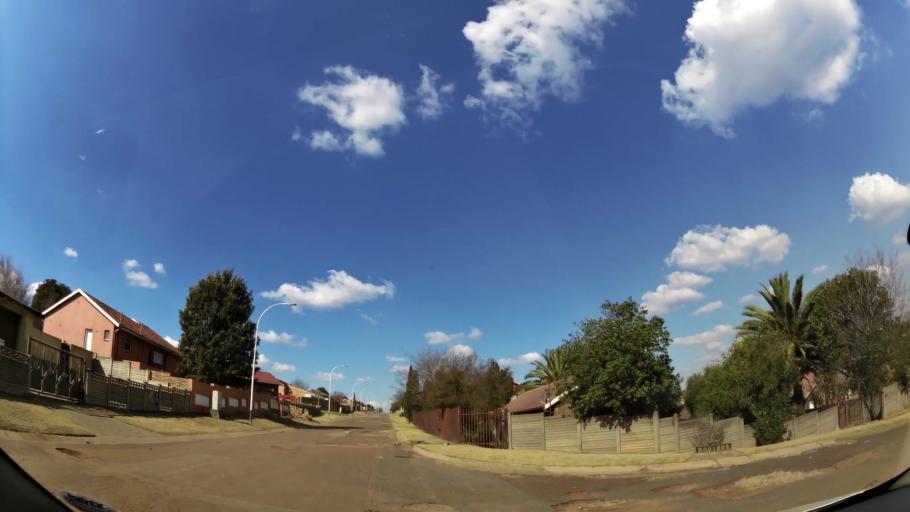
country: ZA
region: Mpumalanga
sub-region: Nkangala District Municipality
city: Witbank
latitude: -25.9300
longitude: 29.2379
